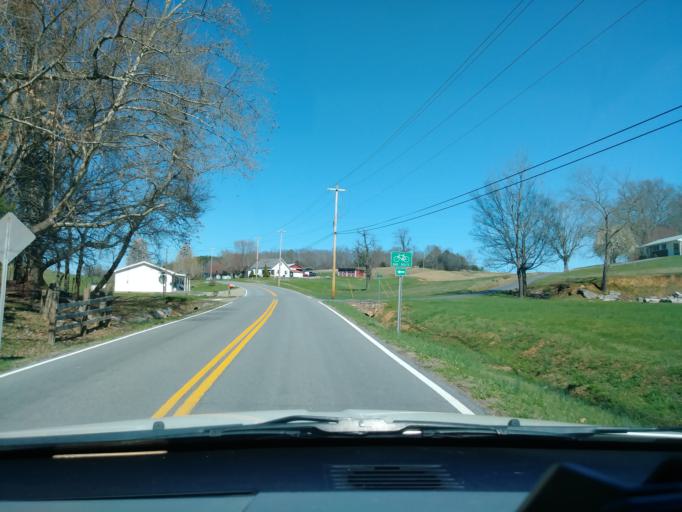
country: US
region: Tennessee
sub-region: Cocke County
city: Newport
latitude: 35.9740
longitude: -83.0593
